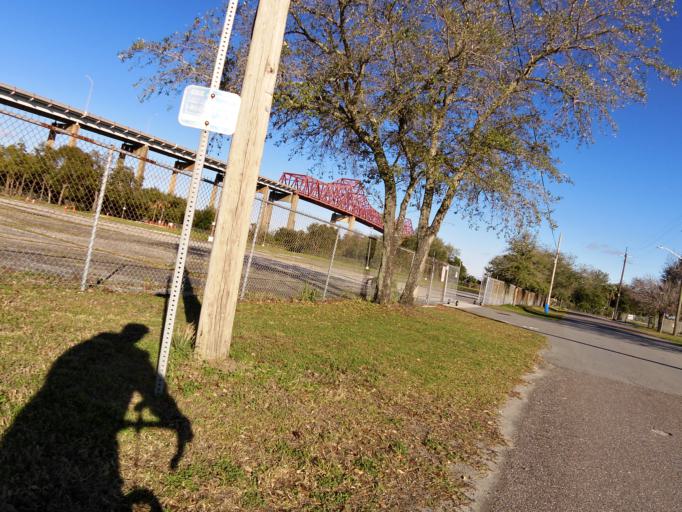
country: US
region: Florida
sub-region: Duval County
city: Jacksonville
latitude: 30.3258
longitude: -81.6299
